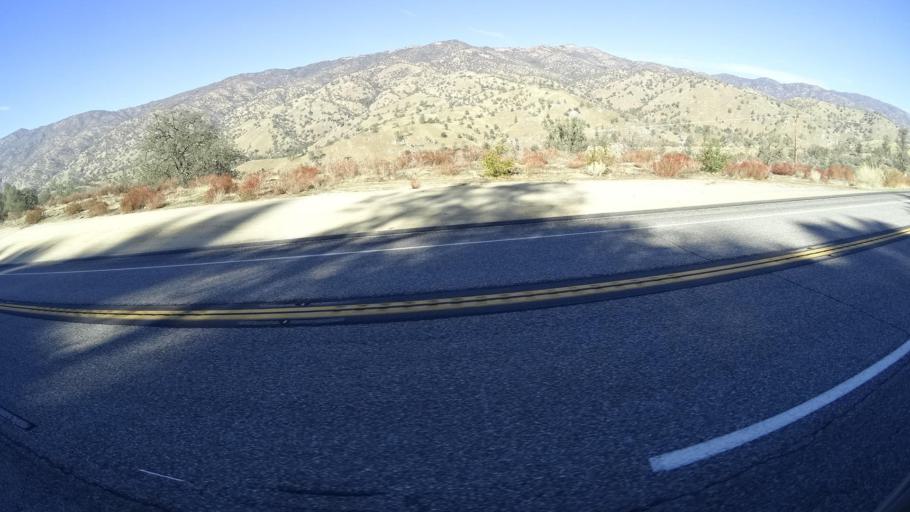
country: US
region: California
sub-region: Kern County
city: Bodfish
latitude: 35.5310
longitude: -118.6344
